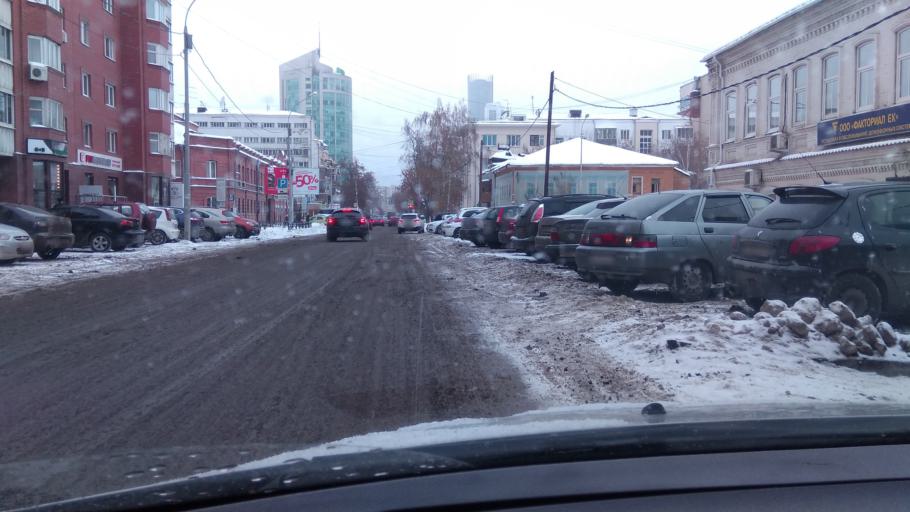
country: RU
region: Sverdlovsk
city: Yekaterinburg
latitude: 56.8317
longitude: 60.5931
